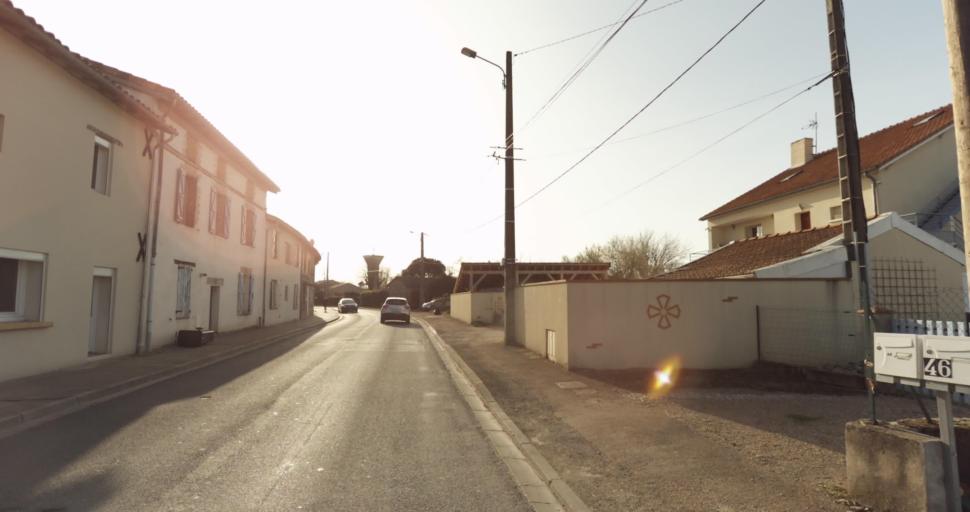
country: FR
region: Midi-Pyrenees
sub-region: Departement du Tarn
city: Saint-Sulpice-la-Pointe
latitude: 43.7697
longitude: 1.6833
